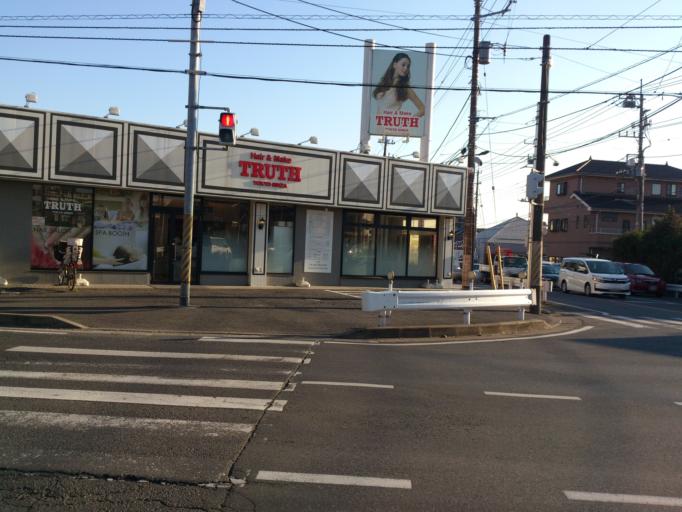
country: JP
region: Chiba
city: Kashiwa
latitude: 35.7957
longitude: 139.9649
